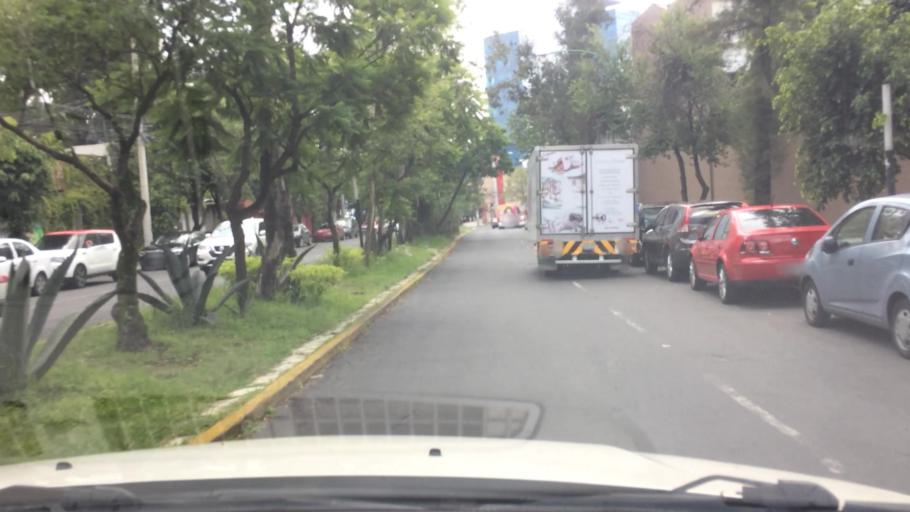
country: MX
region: Mexico City
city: Alvaro Obregon
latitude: 19.3578
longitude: -99.1999
